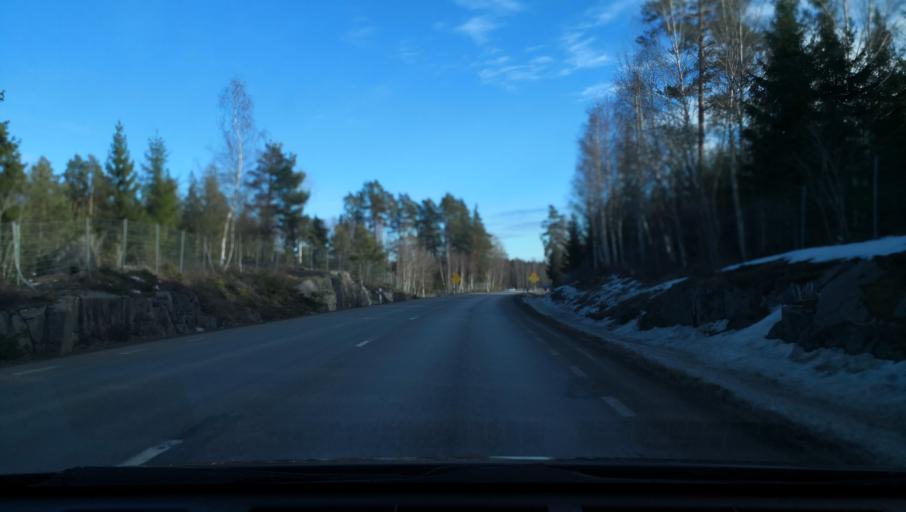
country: SE
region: Uppsala
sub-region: Osthammars Kommun
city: Osterbybruk
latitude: 60.1677
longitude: 17.9682
